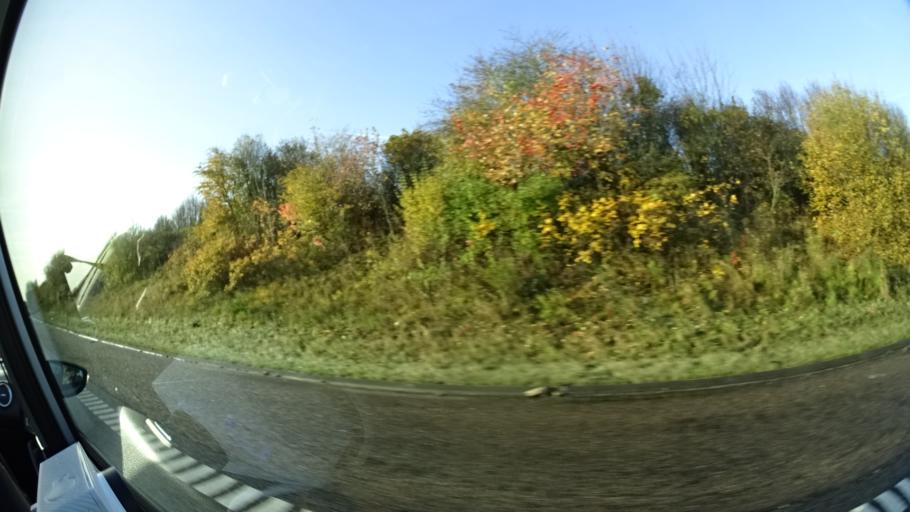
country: DK
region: South Denmark
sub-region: Fredericia Kommune
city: Taulov
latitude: 55.5858
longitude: 9.6084
